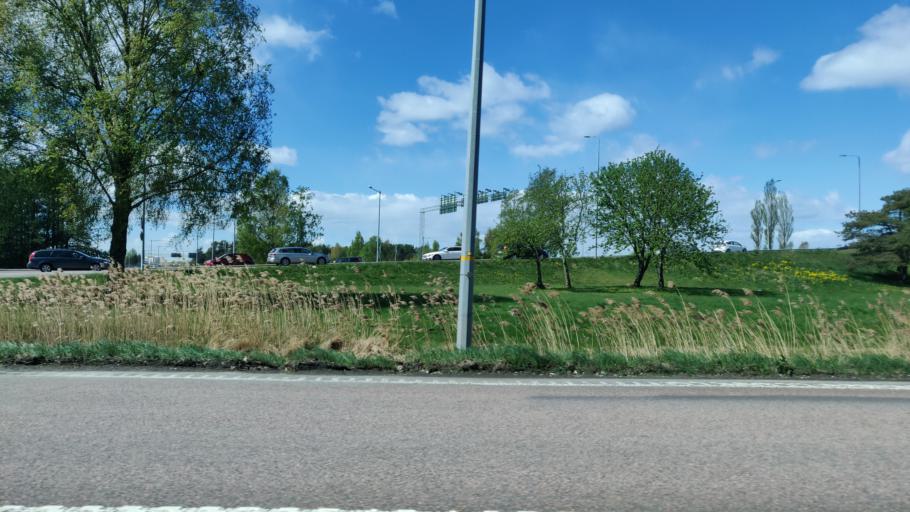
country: SE
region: Vaermland
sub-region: Karlstads Kommun
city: Karlstad
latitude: 59.3837
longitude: 13.4894
